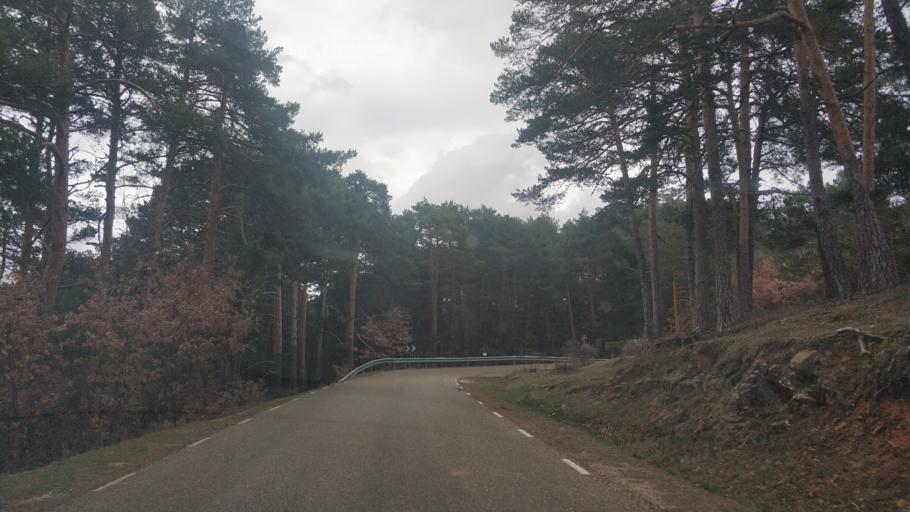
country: ES
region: Castille and Leon
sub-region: Provincia de Burgos
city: Canicosa de la Sierra
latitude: 41.9287
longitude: -3.0409
